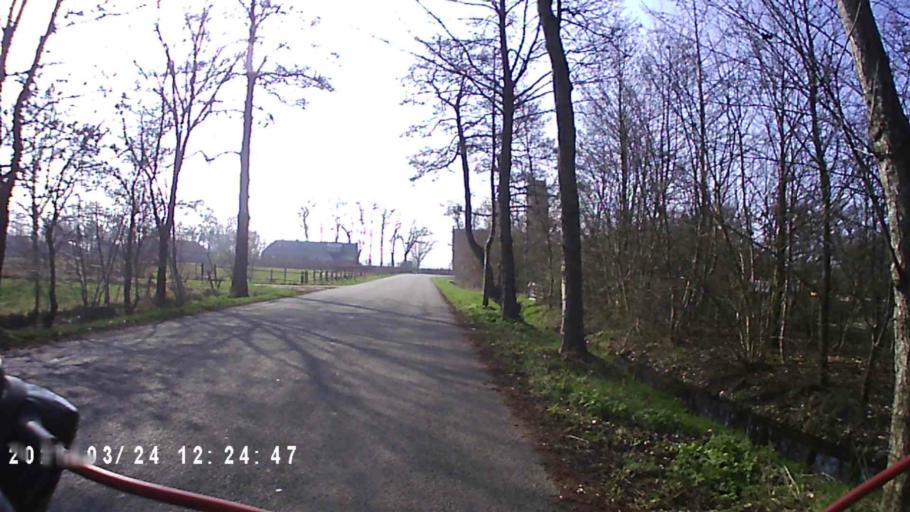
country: NL
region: Groningen
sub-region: Gemeente Leek
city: Leek
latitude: 53.1822
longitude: 6.3930
